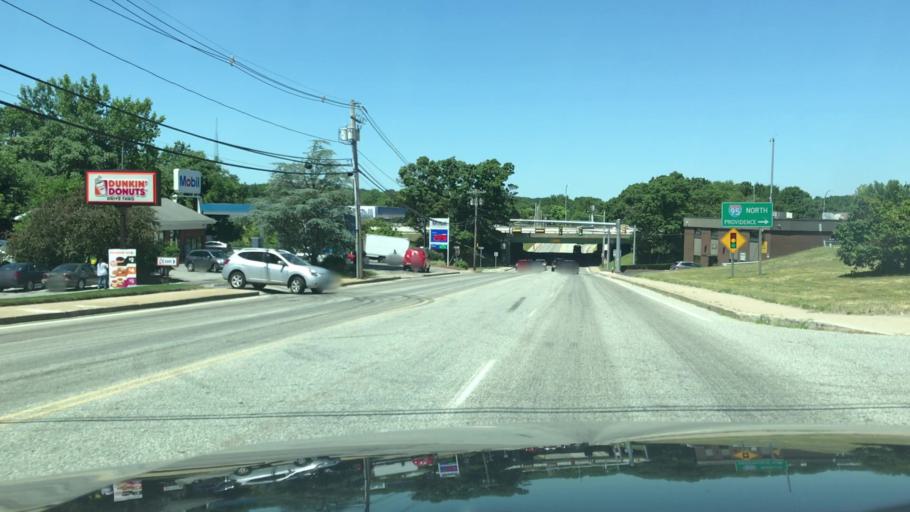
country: US
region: Rhode Island
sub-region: Providence County
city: Cranston
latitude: 41.7530
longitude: -71.4356
